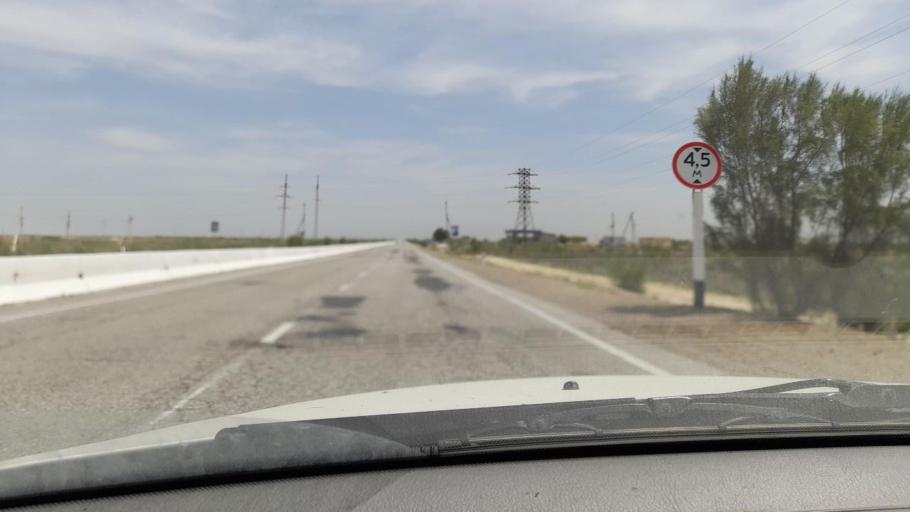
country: UZ
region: Navoiy
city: Qiziltepa
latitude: 40.0836
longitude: 64.9441
